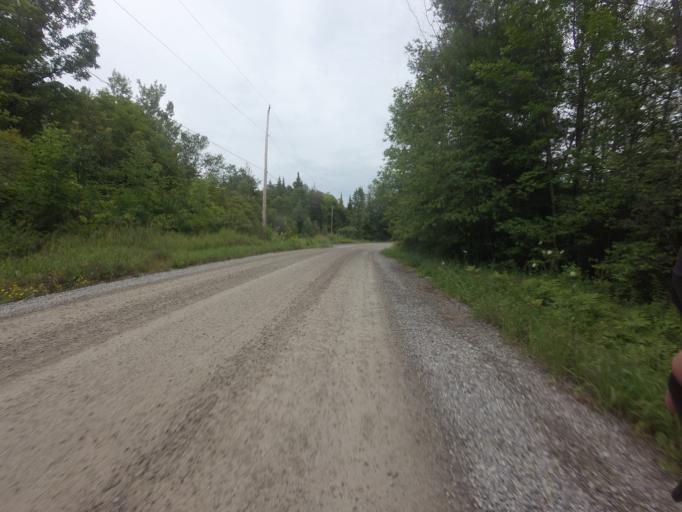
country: CA
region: Ontario
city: Carleton Place
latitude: 45.1577
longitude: -76.1957
